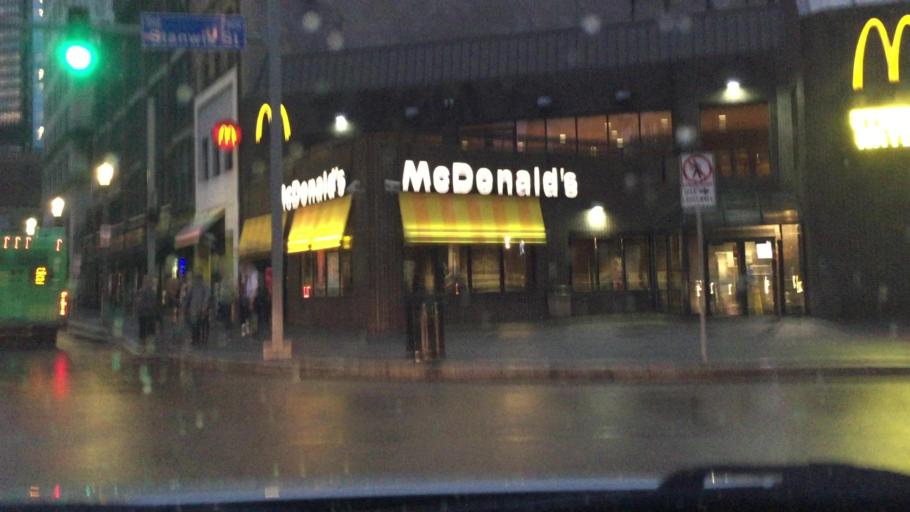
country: US
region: Pennsylvania
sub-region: Allegheny County
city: Pittsburgh
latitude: 40.4413
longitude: -80.0040
